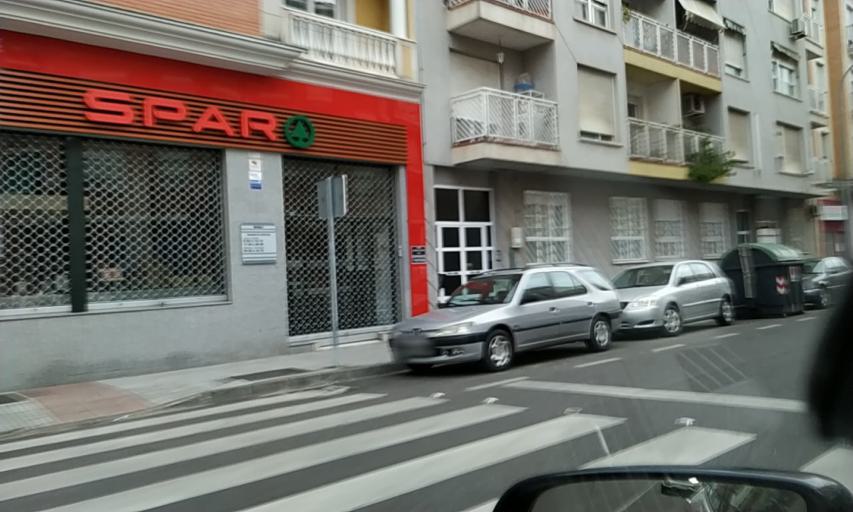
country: ES
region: Extremadura
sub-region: Provincia de Badajoz
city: Badajoz
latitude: 38.8765
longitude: -6.9579
